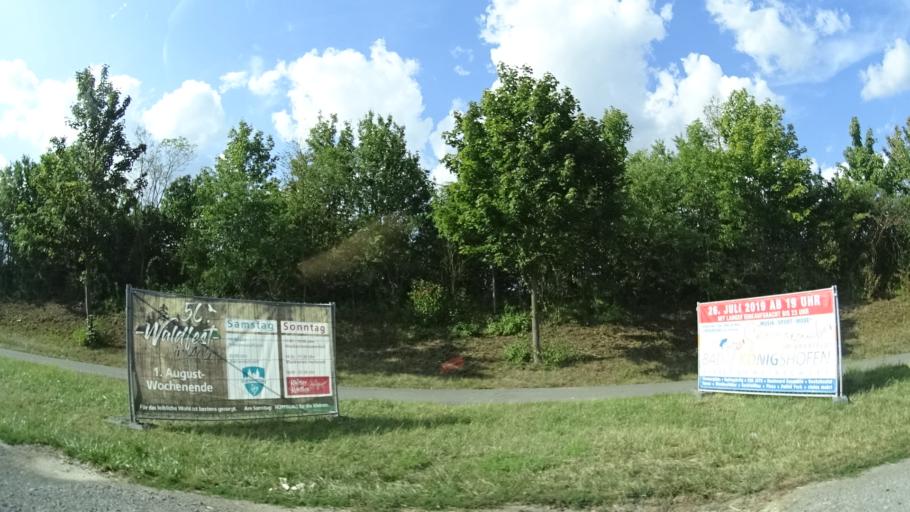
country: DE
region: Bavaria
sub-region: Regierungsbezirk Unterfranken
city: Bad Konigshofen im Grabfeld
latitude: 50.2992
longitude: 10.4598
